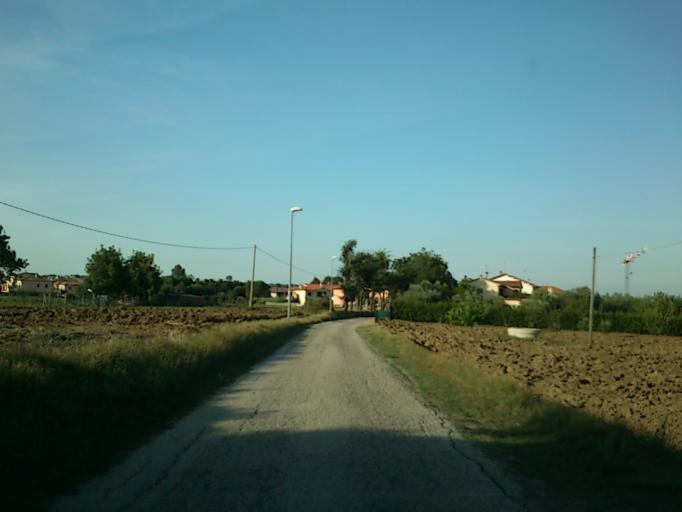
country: IT
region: The Marches
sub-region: Provincia di Pesaro e Urbino
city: Calcinelli
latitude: 43.7692
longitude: 12.9241
